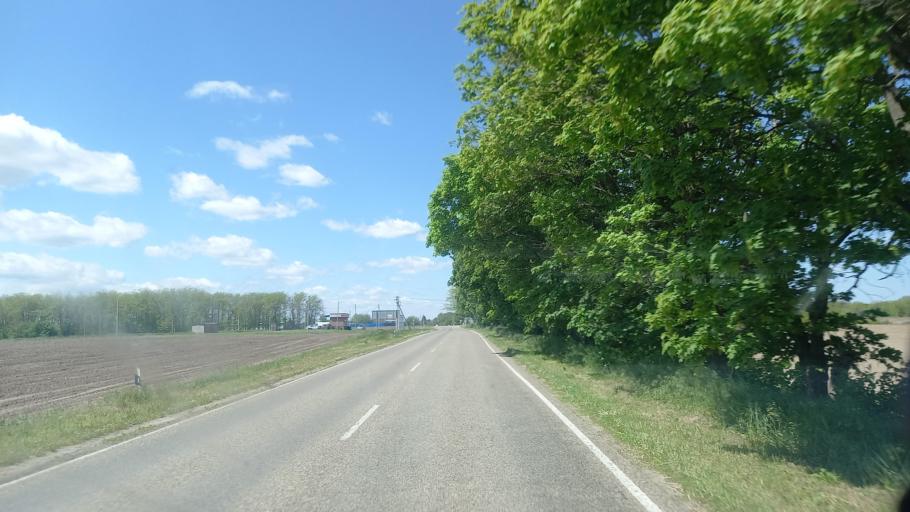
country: RU
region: Krasnodarskiy
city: Kazanskaya
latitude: 45.3644
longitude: 40.3950
